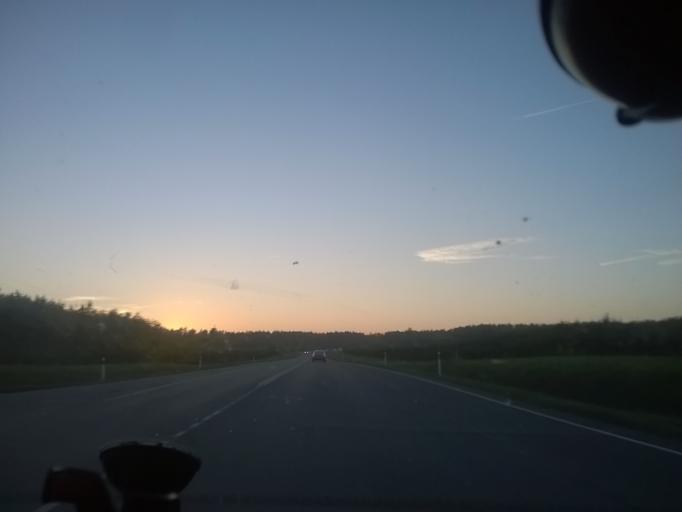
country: EE
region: Laeaene
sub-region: Ridala Parish
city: Uuemoisa
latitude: 58.9568
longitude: 23.7367
